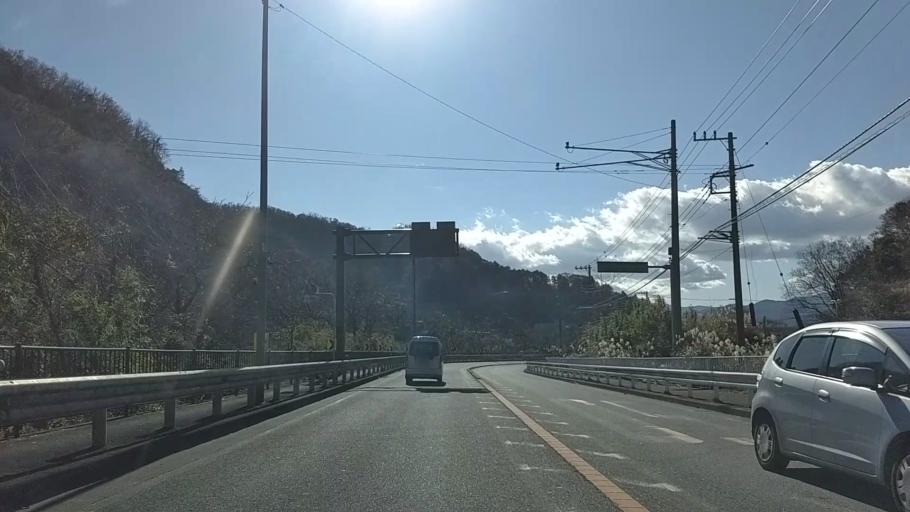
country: JP
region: Kanagawa
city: Hadano
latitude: 35.3563
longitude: 139.1577
